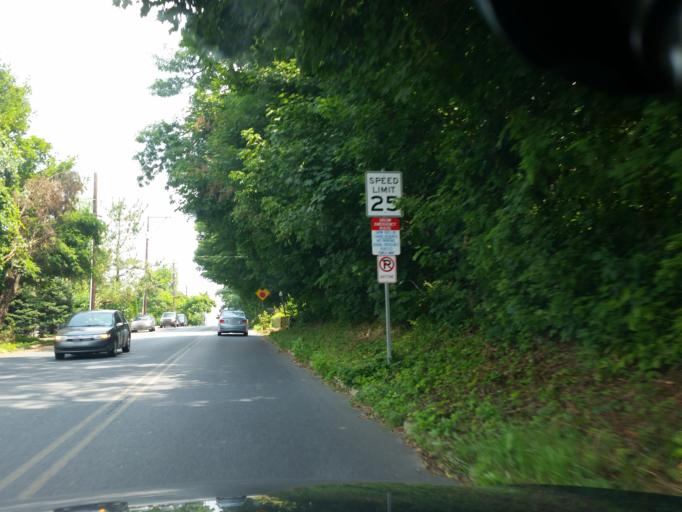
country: US
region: Pennsylvania
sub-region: Cumberland County
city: Enola
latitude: 40.2969
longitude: -76.9347
